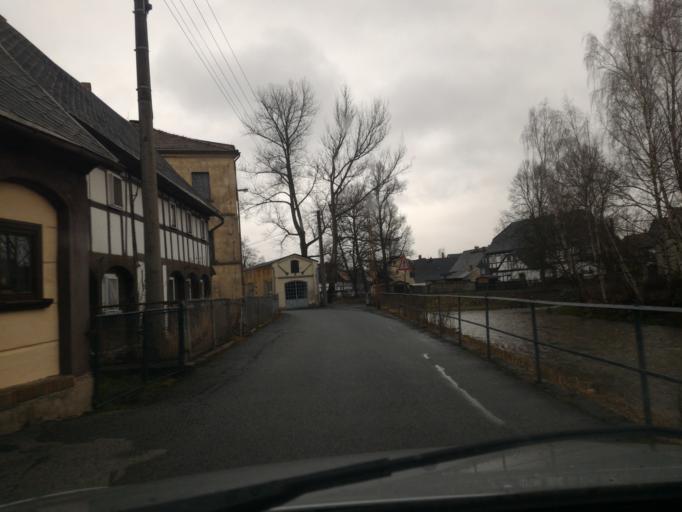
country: DE
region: Saxony
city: Grossschonau
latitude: 50.8996
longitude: 14.6650
